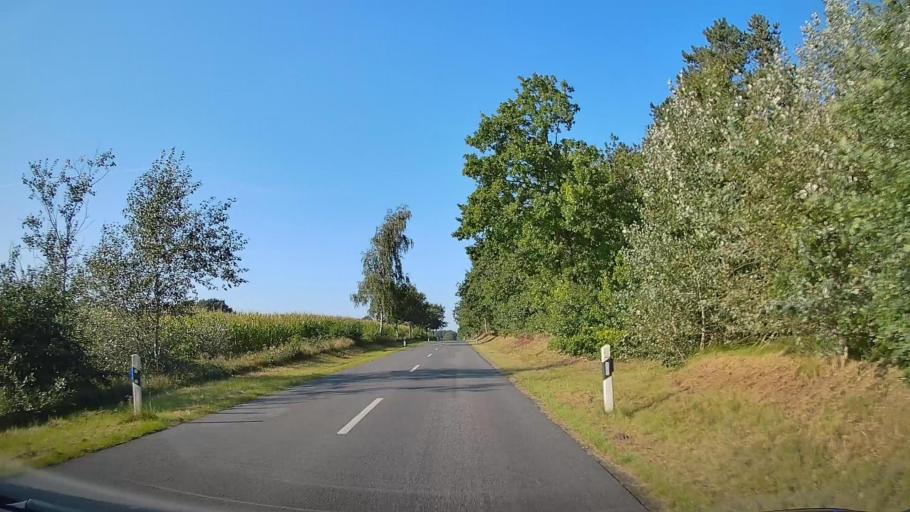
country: DE
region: Lower Saxony
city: Nordholz
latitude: 53.8074
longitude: 8.6017
